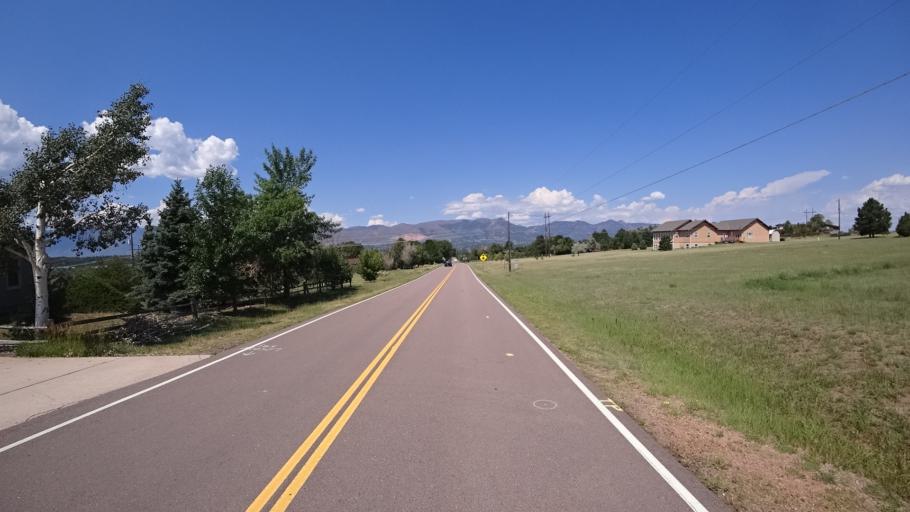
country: US
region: Colorado
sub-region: El Paso County
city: Air Force Academy
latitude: 38.9358
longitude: -104.7826
